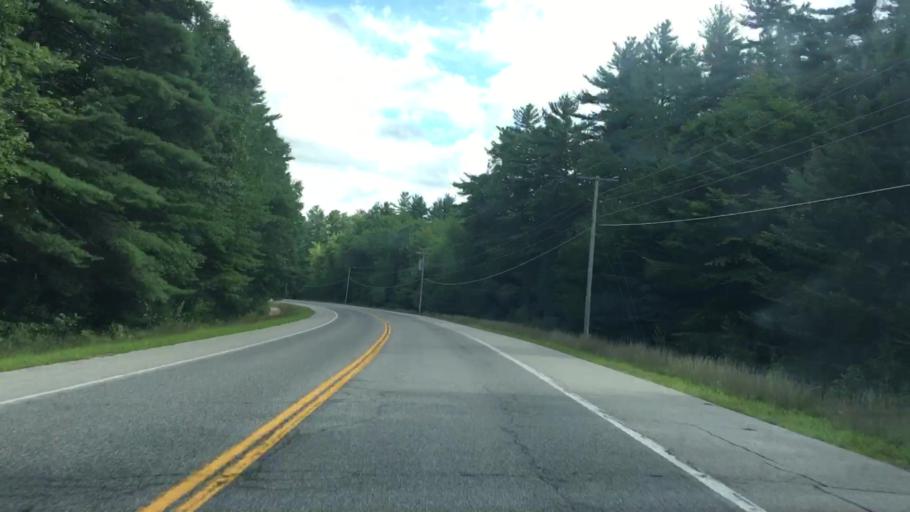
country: US
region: Maine
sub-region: York County
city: South Sanford
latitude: 43.3763
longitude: -70.7398
